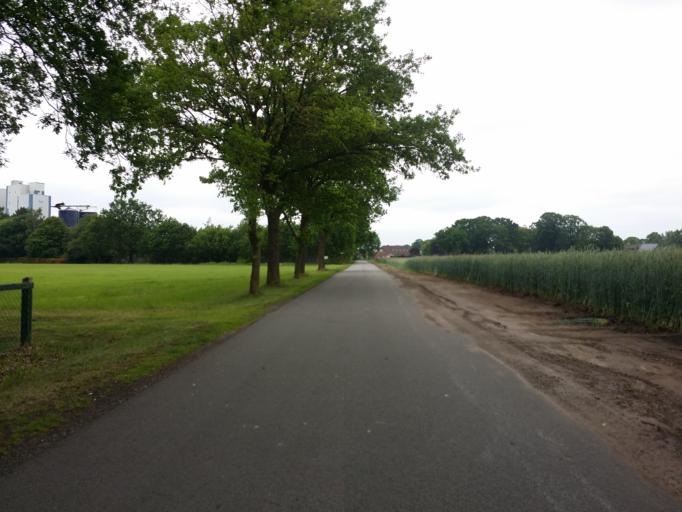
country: DE
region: Lower Saxony
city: Hatten
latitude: 53.0875
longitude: 8.3813
